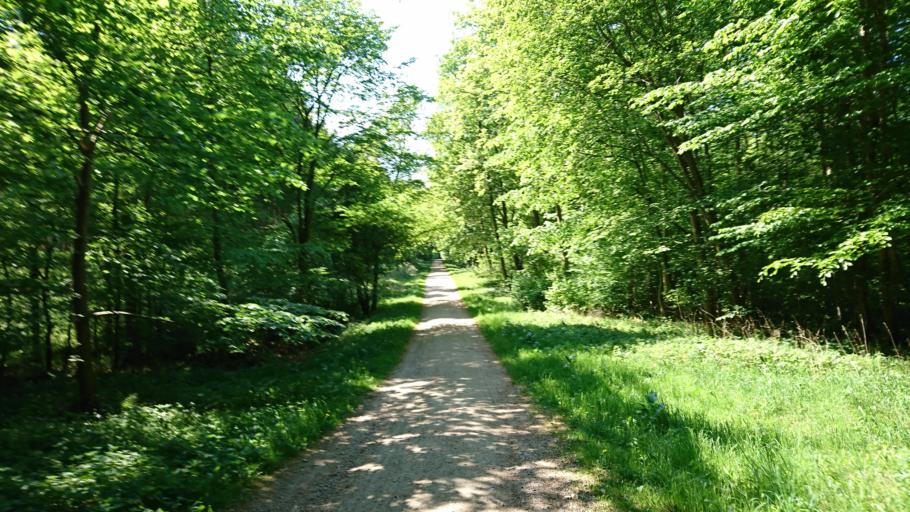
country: DK
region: Capital Region
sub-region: Ballerup Kommune
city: Ballerup
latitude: 55.7570
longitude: 12.3548
